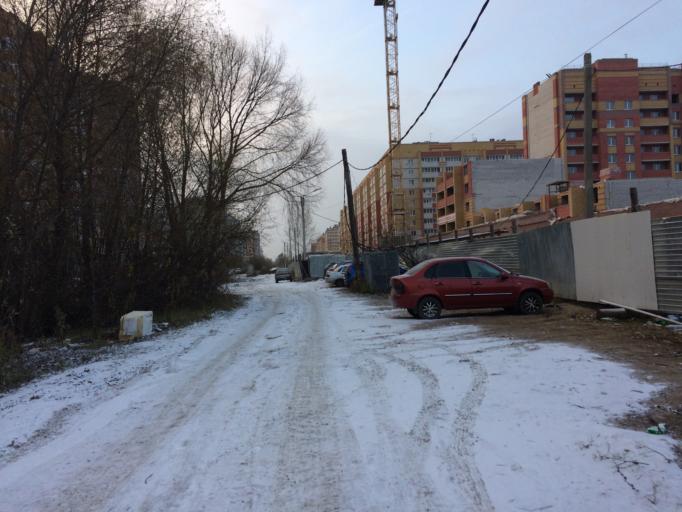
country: RU
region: Mariy-El
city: Yoshkar-Ola
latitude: 56.6382
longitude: 47.9311
